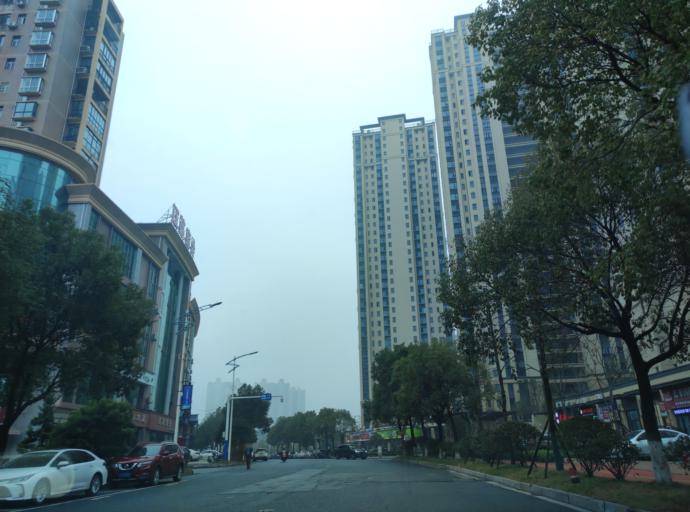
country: CN
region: Jiangxi Sheng
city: Pingxiang
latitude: 27.6661
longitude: 113.8883
